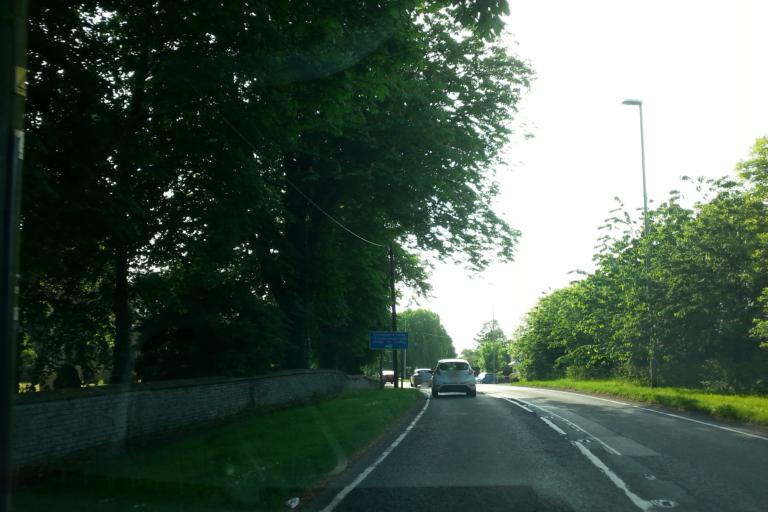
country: GB
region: England
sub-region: Cambridgeshire
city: Earith
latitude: 52.3512
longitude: 0.0143
